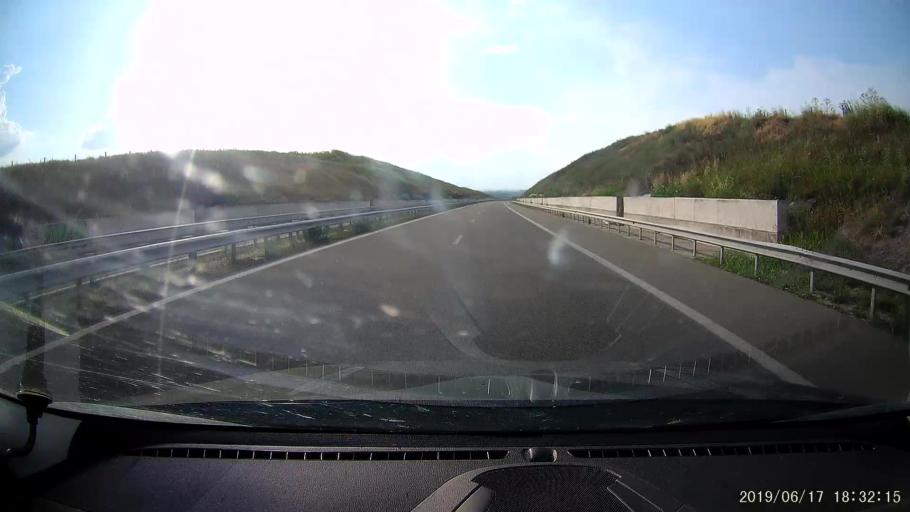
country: BG
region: Khaskovo
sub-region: Obshtina Dimitrovgrad
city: Dimitrovgrad
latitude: 42.0568
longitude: 25.4834
